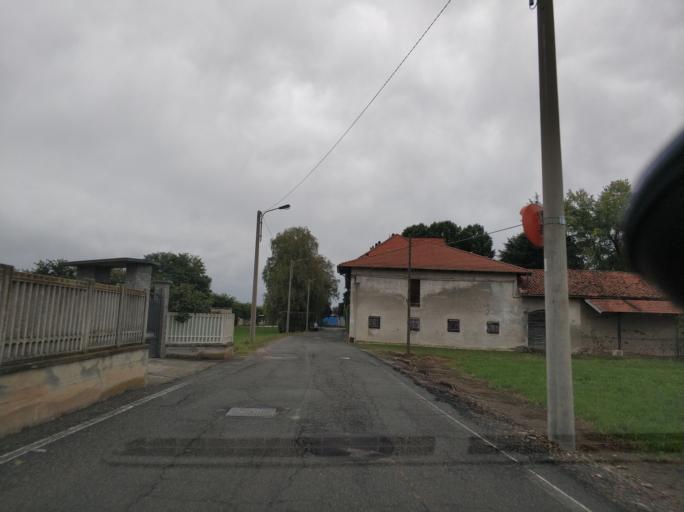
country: IT
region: Piedmont
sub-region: Provincia di Torino
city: Cirie
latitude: 45.2139
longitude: 7.6060
